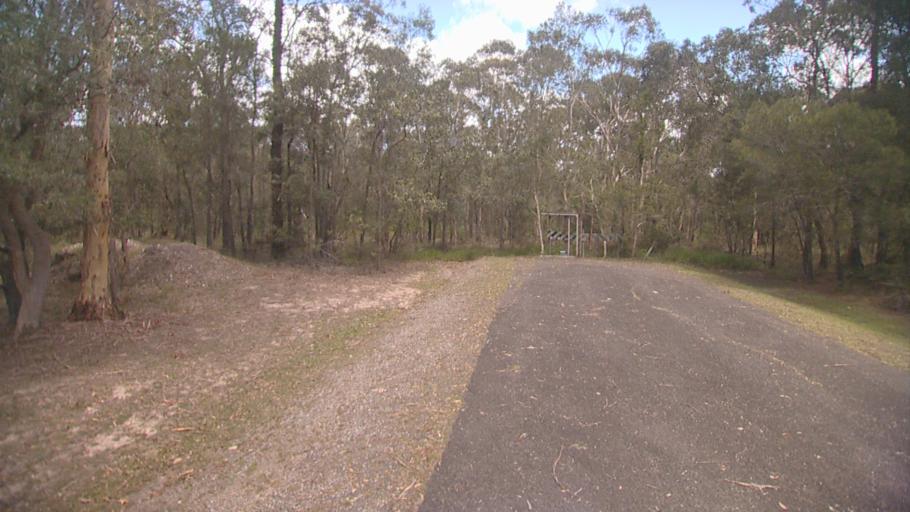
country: AU
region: Queensland
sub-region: Redland
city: Redland Bay
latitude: -27.6514
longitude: 153.2432
